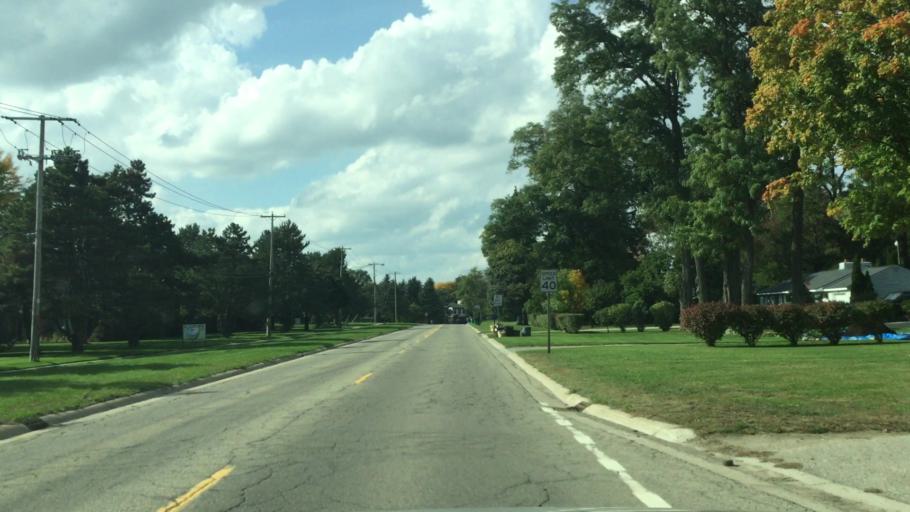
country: US
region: Michigan
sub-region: Oakland County
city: Waterford
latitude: 42.6547
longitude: -83.4386
